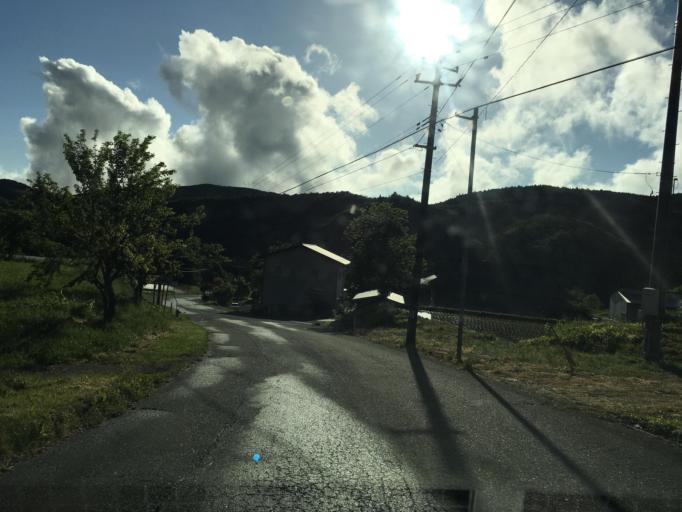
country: JP
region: Iwate
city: Ichinoseki
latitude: 38.8638
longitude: 141.4307
